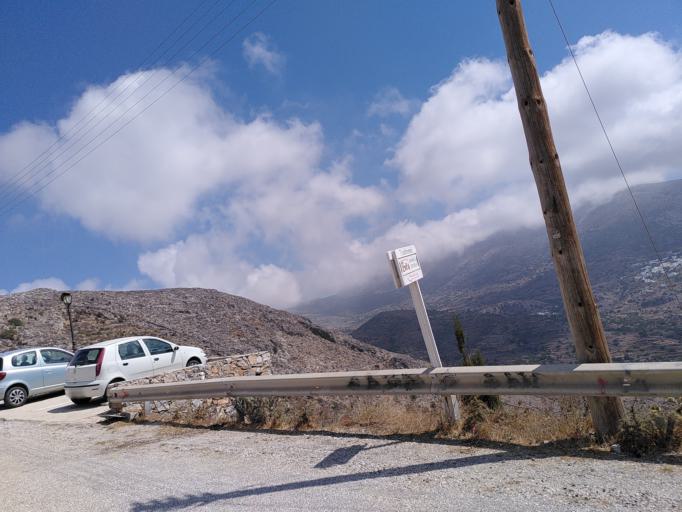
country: GR
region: South Aegean
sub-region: Nomos Kykladon
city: Amorgos
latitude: 36.9162
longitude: 25.9834
